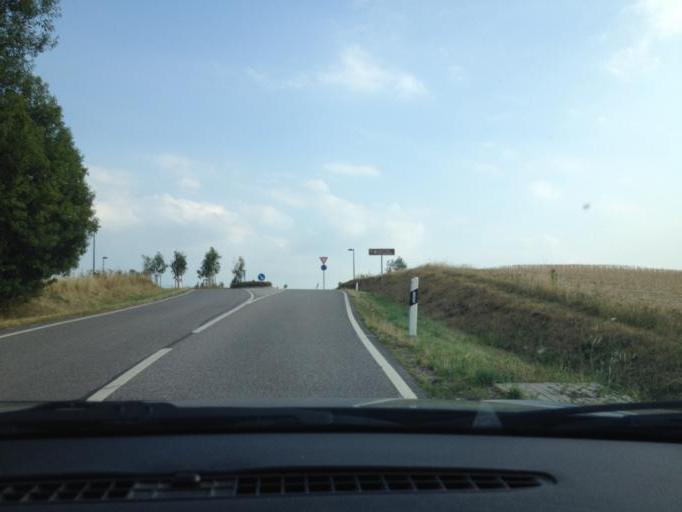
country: DE
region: Rheinland-Pfalz
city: Achtelsbach
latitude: 49.5774
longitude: 7.0729
